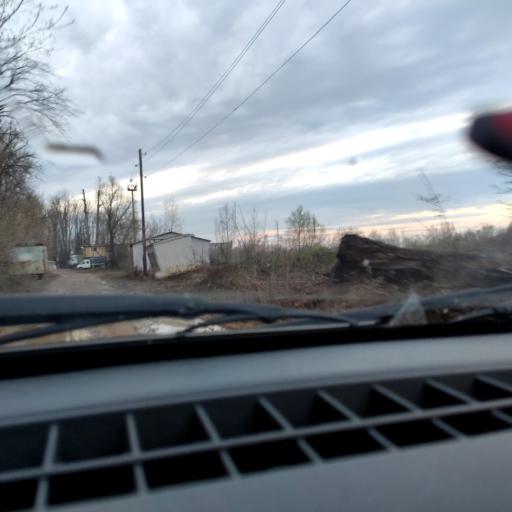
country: RU
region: Bashkortostan
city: Ufa
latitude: 54.6759
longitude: 55.9507
